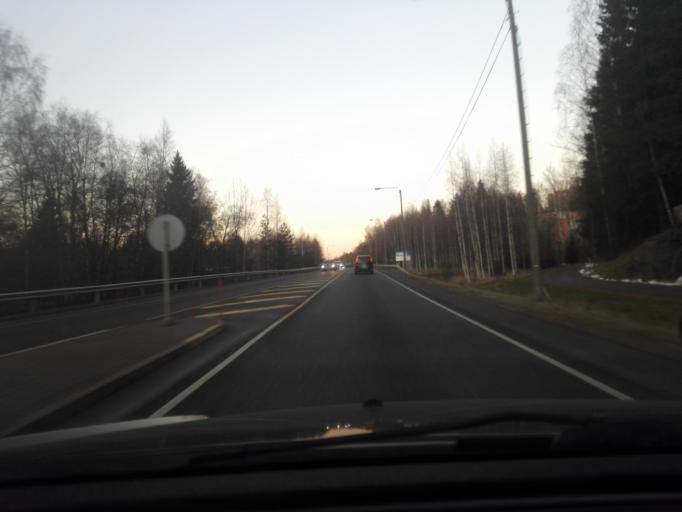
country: FI
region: Uusimaa
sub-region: Helsinki
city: Vantaa
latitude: 60.2760
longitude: 25.0963
